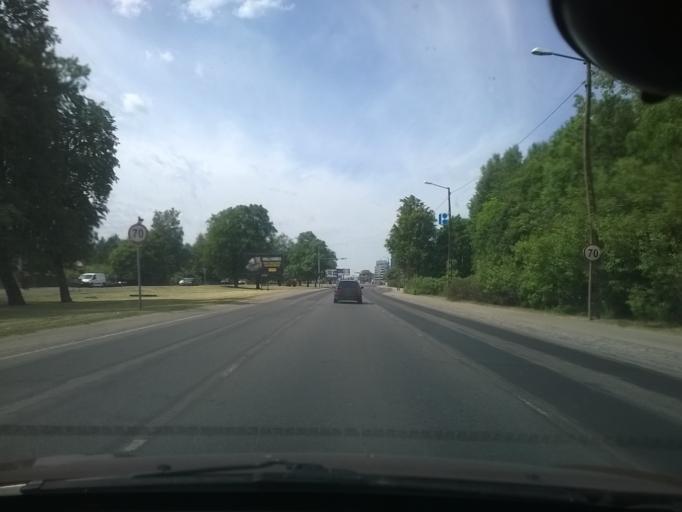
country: EE
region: Harju
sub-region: Tallinna linn
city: Tallinn
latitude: 59.4284
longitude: 24.6758
